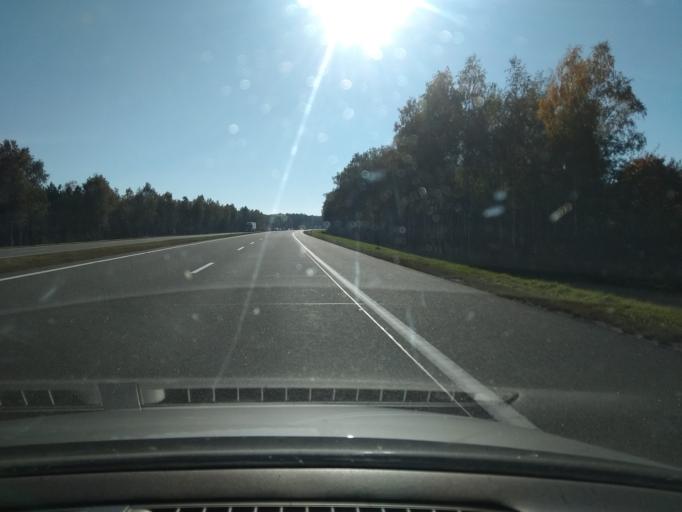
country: BY
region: Brest
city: Baranovichi
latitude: 53.0726
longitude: 25.8815
